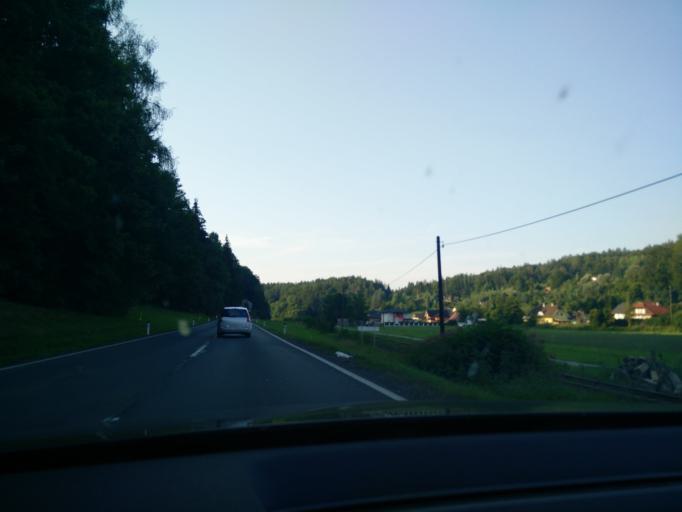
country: AT
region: Carinthia
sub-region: Politischer Bezirk Klagenfurt Land
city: Maria Rain
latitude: 46.5695
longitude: 14.2856
